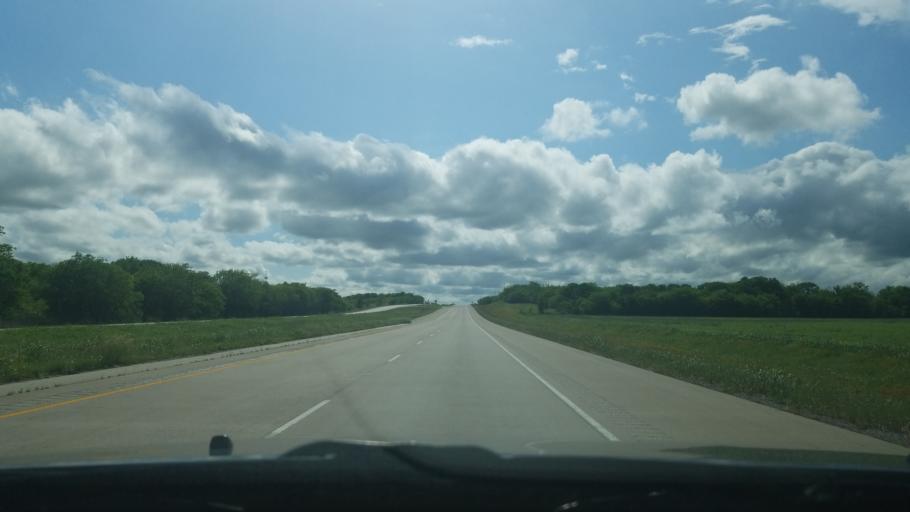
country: US
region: Texas
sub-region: Wise County
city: Decatur
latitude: 33.2458
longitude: -97.4559
